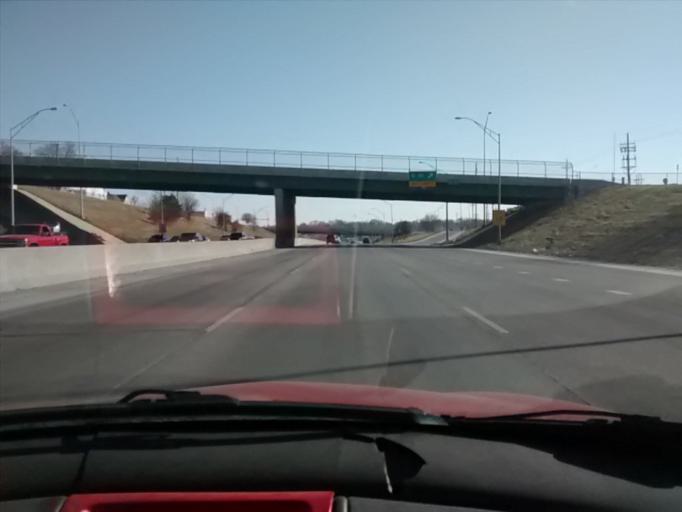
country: US
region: Nebraska
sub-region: Douglas County
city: Omaha
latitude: 41.2091
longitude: -95.9494
